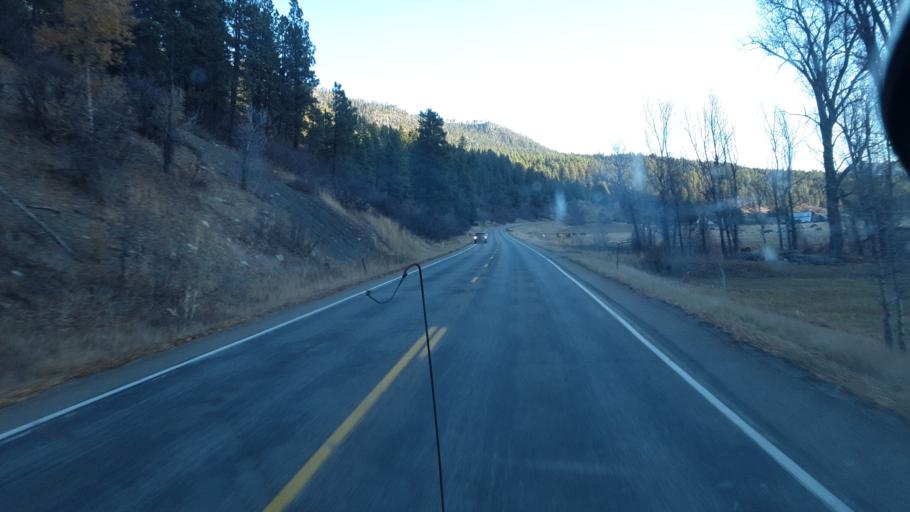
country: US
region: Colorado
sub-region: La Plata County
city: Bayfield
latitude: 37.3397
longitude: -107.7227
